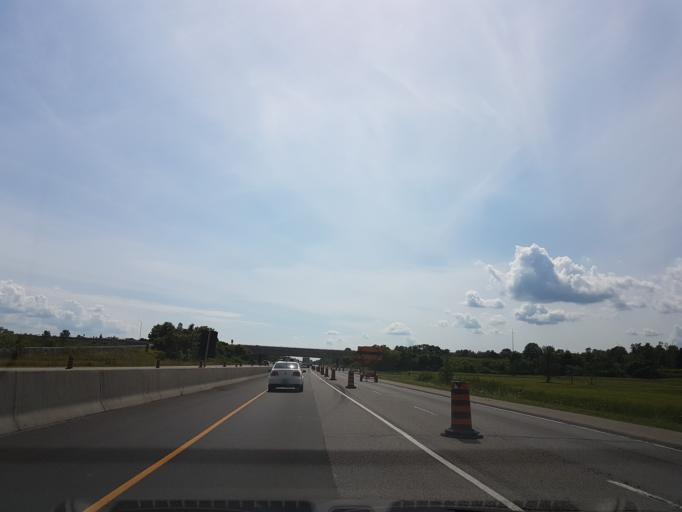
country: CA
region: Ontario
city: Prescott
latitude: 44.7560
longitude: -75.4762
